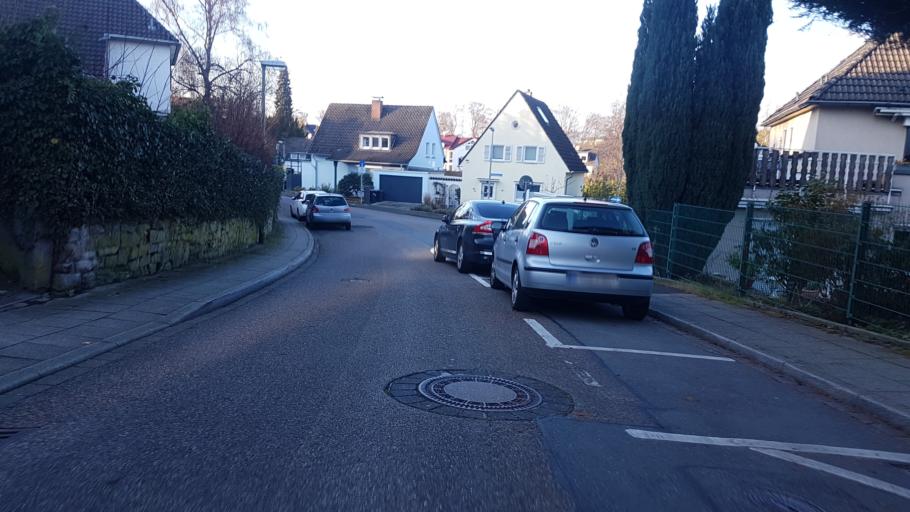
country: DE
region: North Rhine-Westphalia
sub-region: Regierungsbezirk Dusseldorf
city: Essen
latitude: 51.4260
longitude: 7.0343
